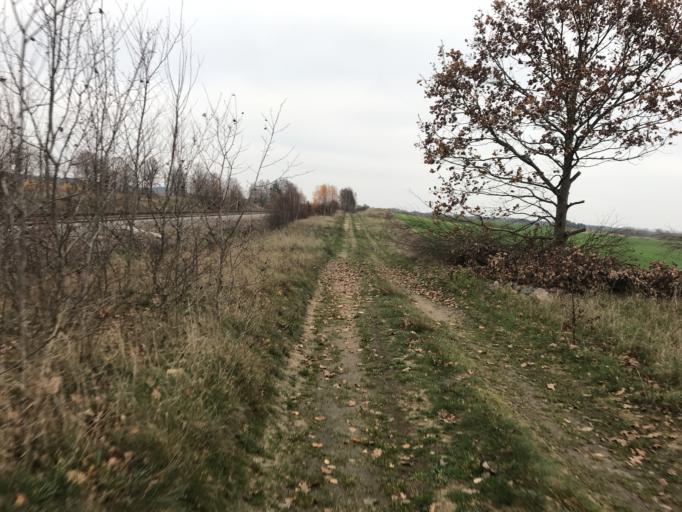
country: PL
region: West Pomeranian Voivodeship
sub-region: Powiat szczecinecki
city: Lubowo
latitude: 53.5887
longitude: 16.4020
